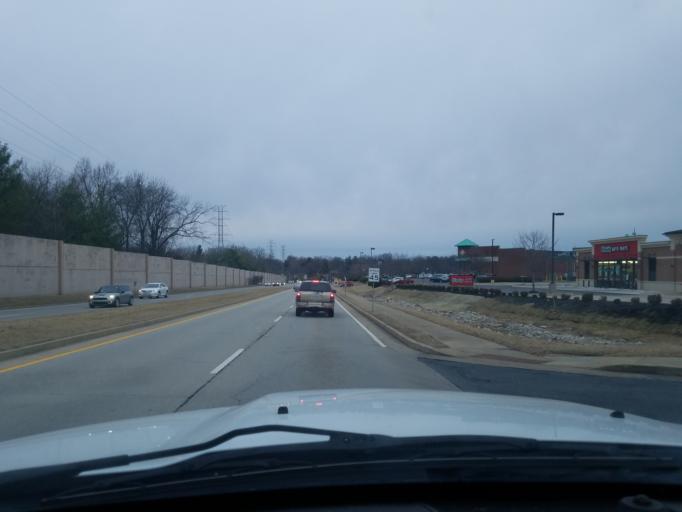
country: US
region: Kentucky
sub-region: Jefferson County
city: Douglass Hills
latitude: 38.2403
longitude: -85.5454
